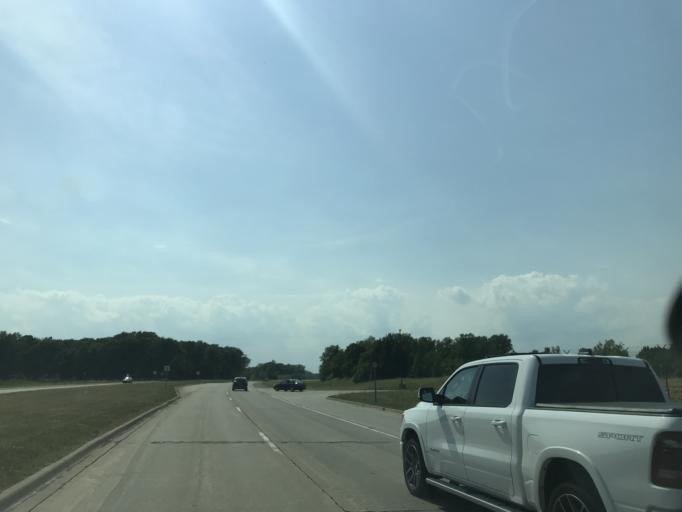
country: US
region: Michigan
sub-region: Wayne County
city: Romulus
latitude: 42.1912
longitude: -83.3559
